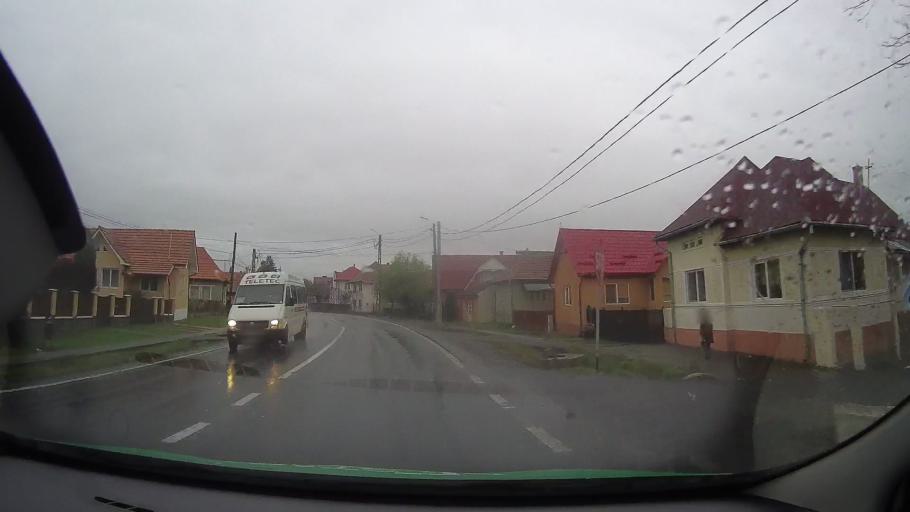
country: RO
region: Mures
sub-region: Comuna Brancovenesti
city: Brancovenesti
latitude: 46.8560
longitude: 24.7586
